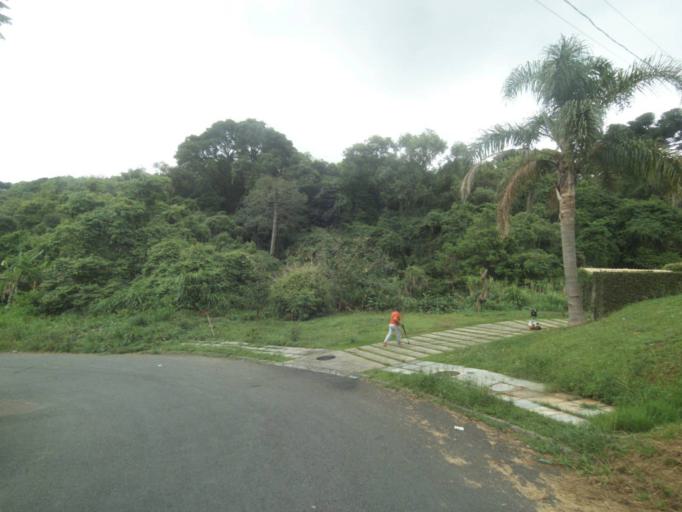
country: BR
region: Parana
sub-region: Curitiba
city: Curitiba
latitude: -25.3854
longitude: -49.2892
